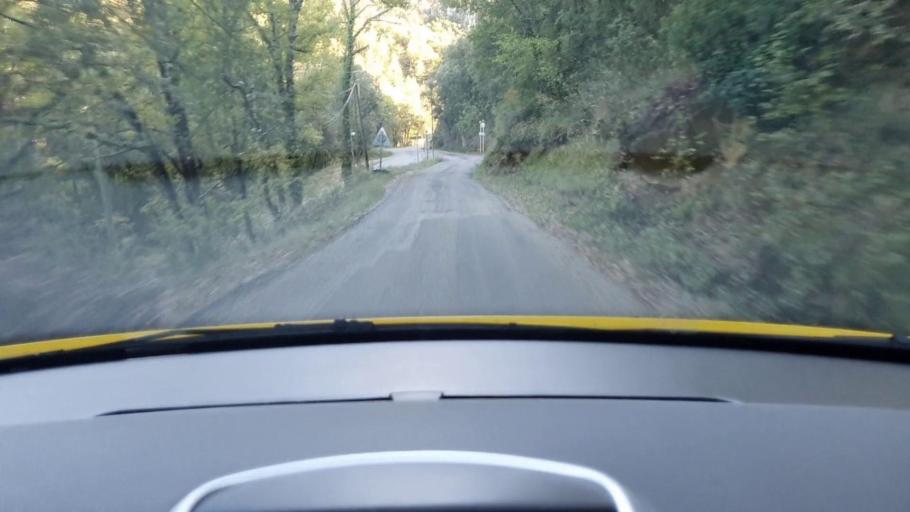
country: FR
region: Languedoc-Roussillon
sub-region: Departement du Gard
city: Saint-Hippolyte-du-Fort
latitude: 43.9670
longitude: 3.8098
